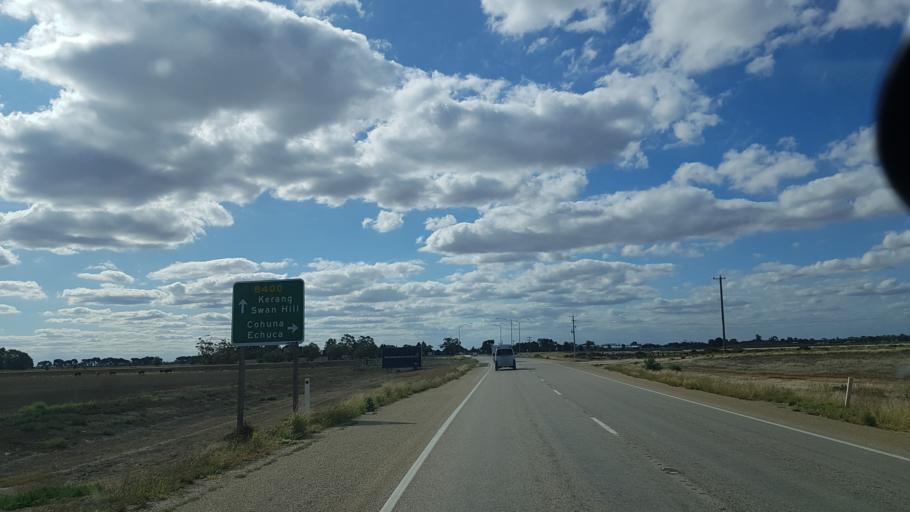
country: AU
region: Victoria
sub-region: Swan Hill
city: Swan Hill
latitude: -35.7653
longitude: 143.9321
